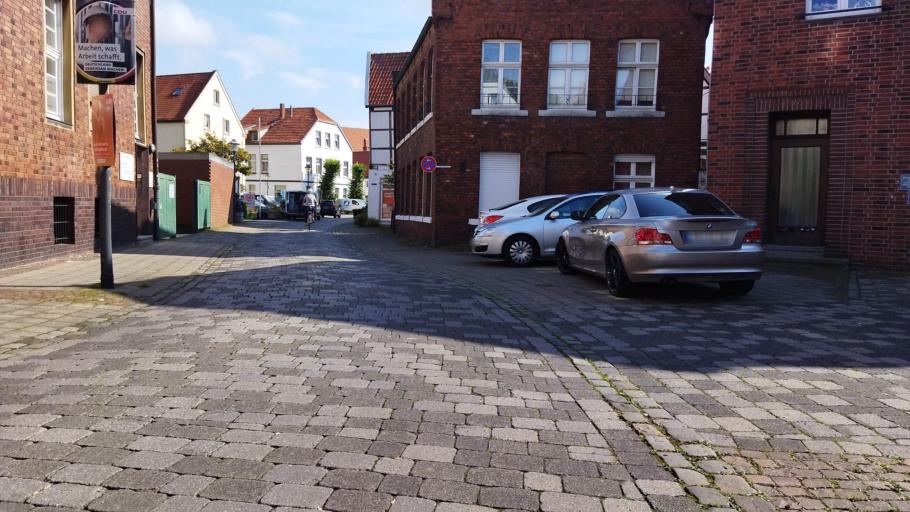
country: DE
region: North Rhine-Westphalia
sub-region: Regierungsbezirk Munster
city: Warendorf
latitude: 51.9507
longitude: 7.9887
